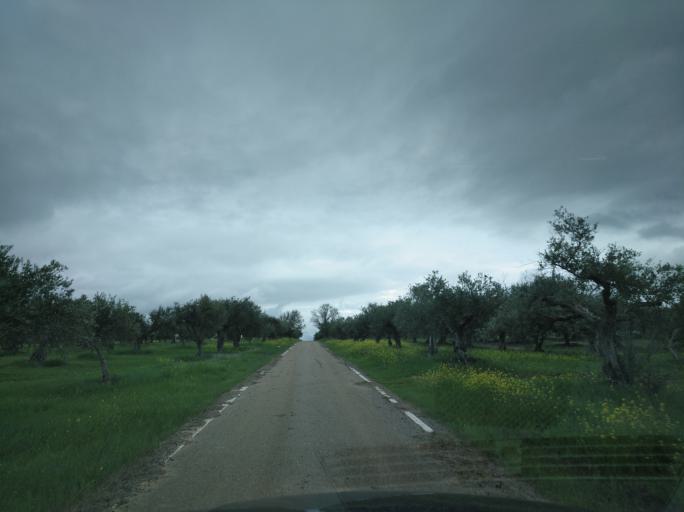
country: PT
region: Portalegre
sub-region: Campo Maior
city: Campo Maior
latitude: 38.9788
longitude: -7.0305
